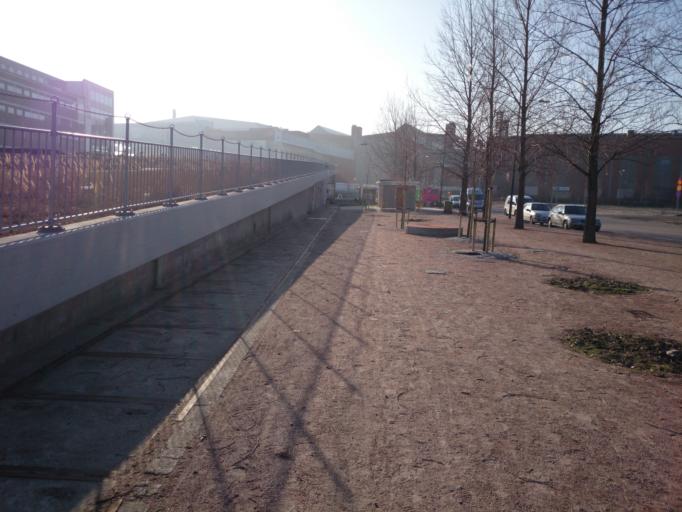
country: SE
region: Skane
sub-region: Malmo
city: Malmoe
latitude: 55.6125
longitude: 12.9845
